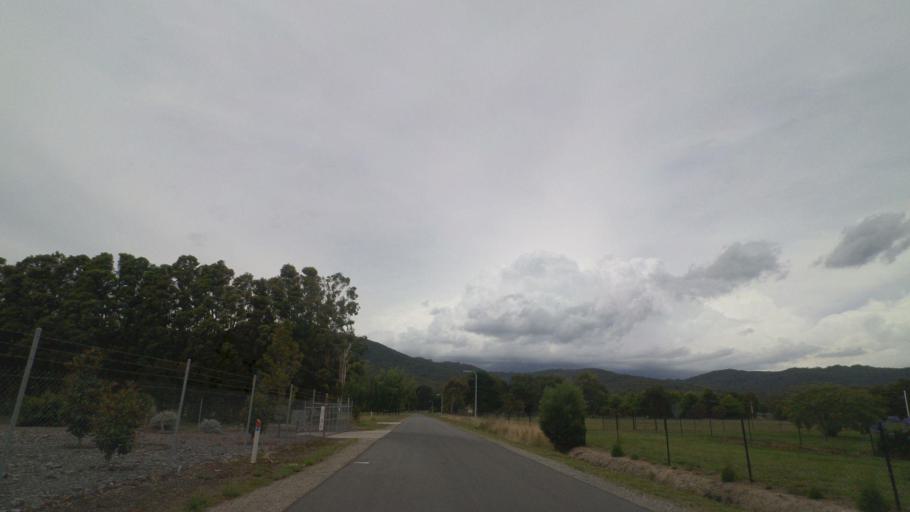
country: AU
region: Victoria
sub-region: Knox
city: The Basin
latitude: -37.8405
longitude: 145.3197
